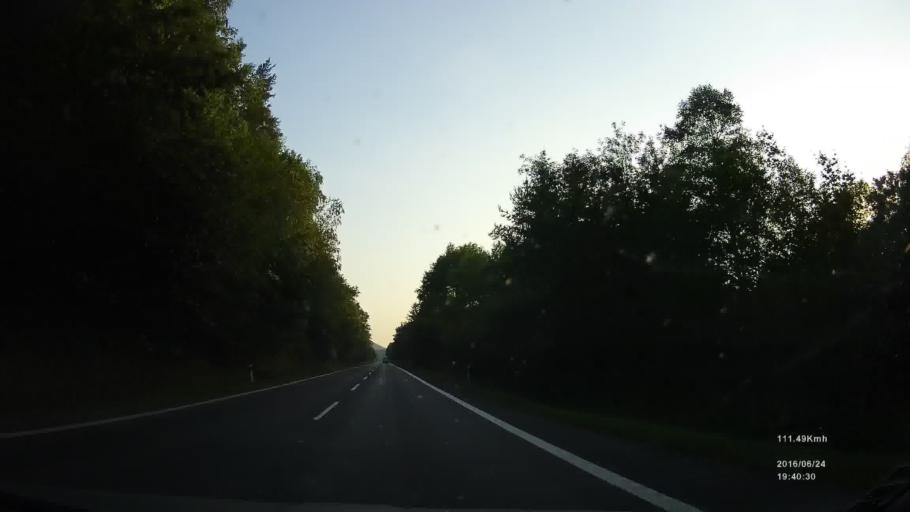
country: SK
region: Banskobystricky
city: Hrochot,Slovakia
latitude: 48.7907
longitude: 19.3598
